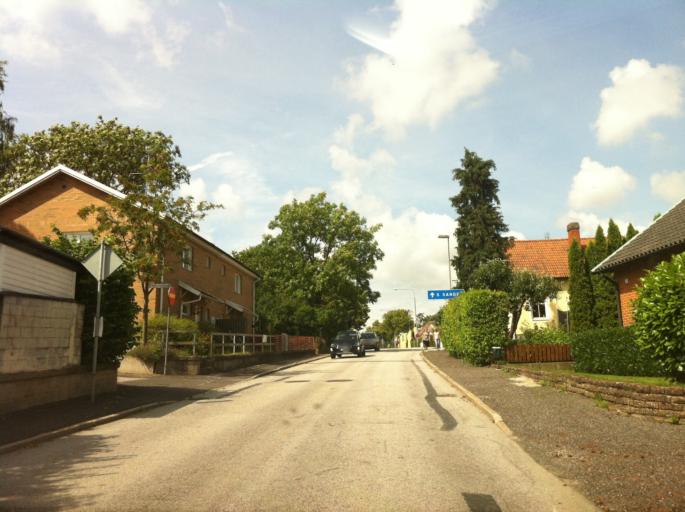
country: SE
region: Skane
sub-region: Lunds Kommun
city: Genarp
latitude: 55.5153
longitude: 13.4181
